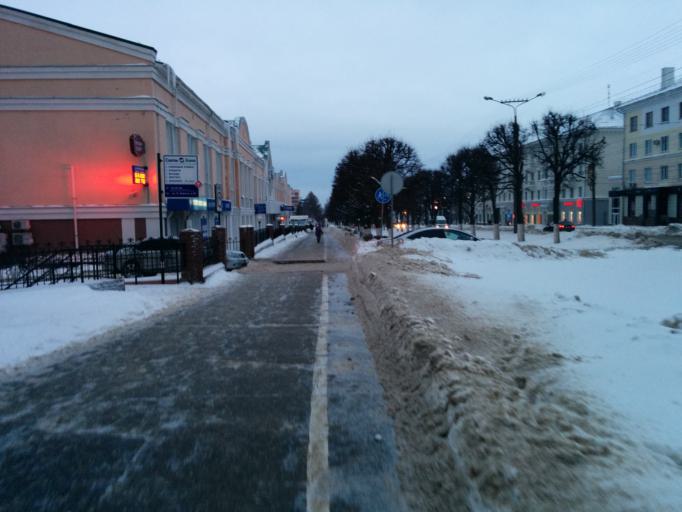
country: RU
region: Chuvashia
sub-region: Cheboksarskiy Rayon
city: Cheboksary
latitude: 56.1323
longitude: 47.2457
